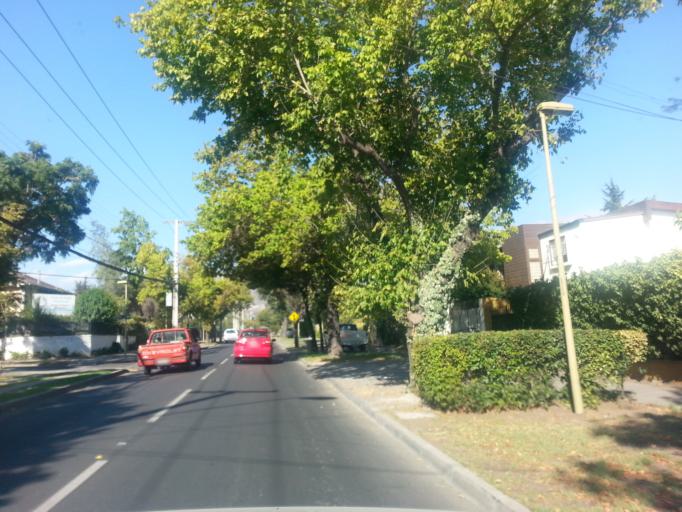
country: CL
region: Santiago Metropolitan
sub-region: Provincia de Santiago
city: Villa Presidente Frei, Nunoa, Santiago, Chile
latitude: -33.4257
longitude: -70.5682
